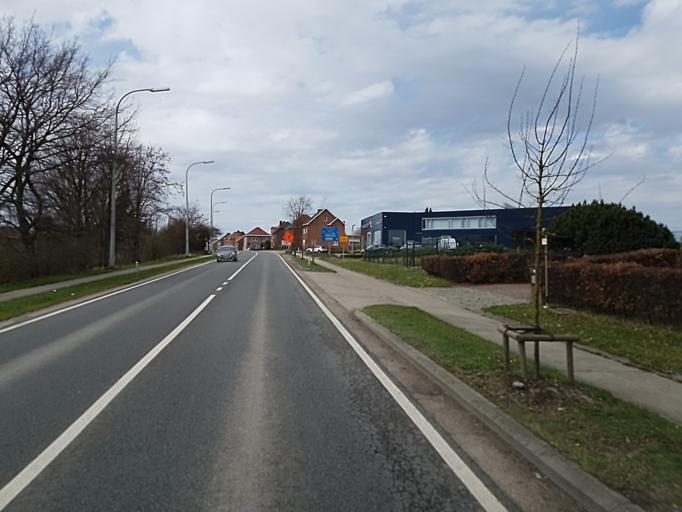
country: BE
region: Flanders
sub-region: Provincie Limburg
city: Borgloon
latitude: 50.7963
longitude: 5.3655
